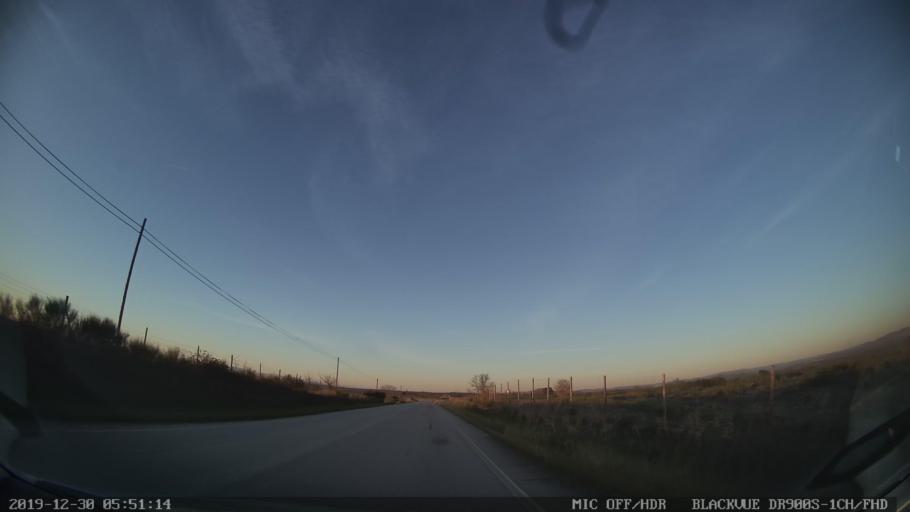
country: PT
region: Castelo Branco
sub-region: Idanha-A-Nova
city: Idanha-a-Nova
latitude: 39.9925
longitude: -7.2433
